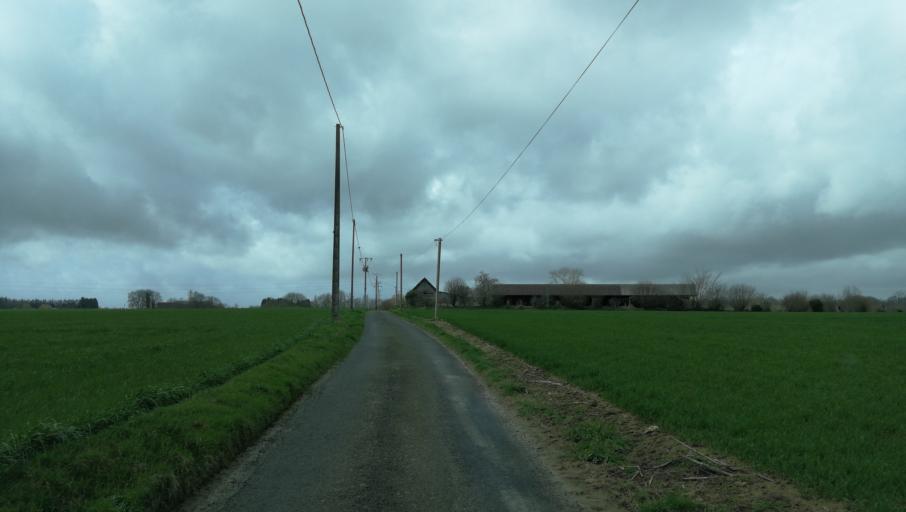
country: FR
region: Haute-Normandie
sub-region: Departement de l'Eure
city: Lieurey
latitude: 49.2330
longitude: 0.5332
